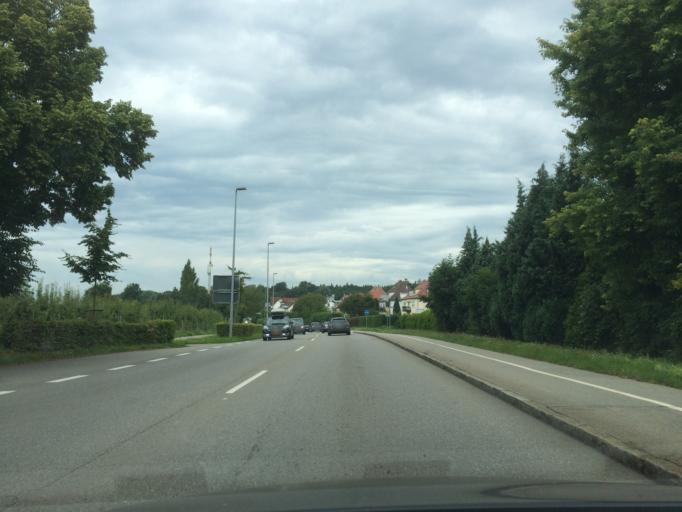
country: DE
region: Baden-Wuerttemberg
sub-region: Tuebingen Region
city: Friedrichshafen
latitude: 47.6587
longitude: 9.4468
